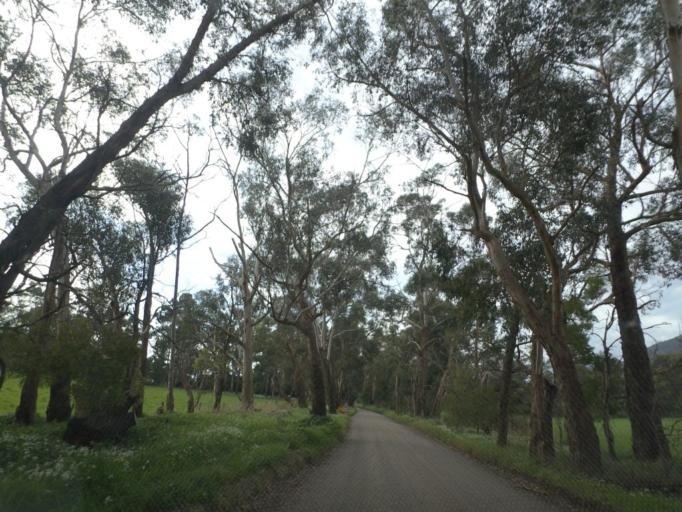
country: AU
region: Victoria
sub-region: Knox
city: The Basin
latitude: -37.8480
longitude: 145.3257
